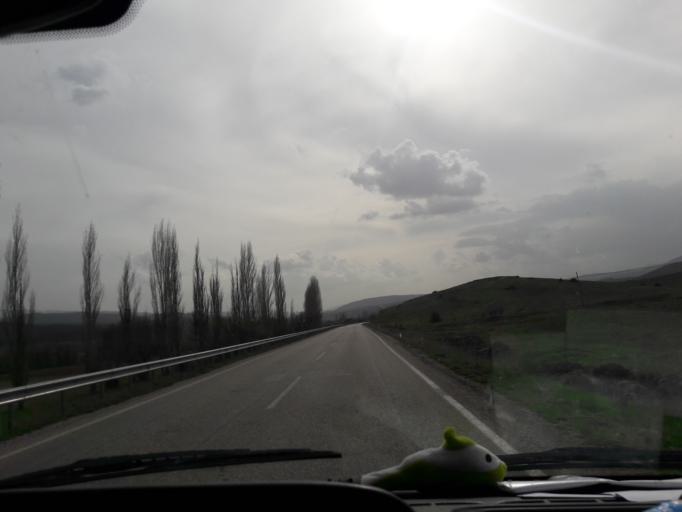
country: TR
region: Gumushane
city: Siran
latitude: 40.1639
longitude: 39.0453
